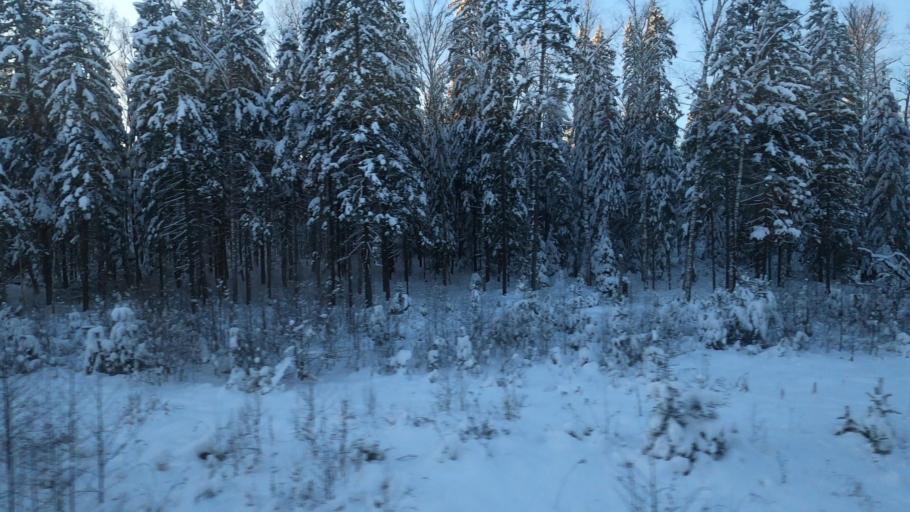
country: RU
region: Moskovskaya
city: Zhukovka
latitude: 56.4957
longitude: 37.5518
